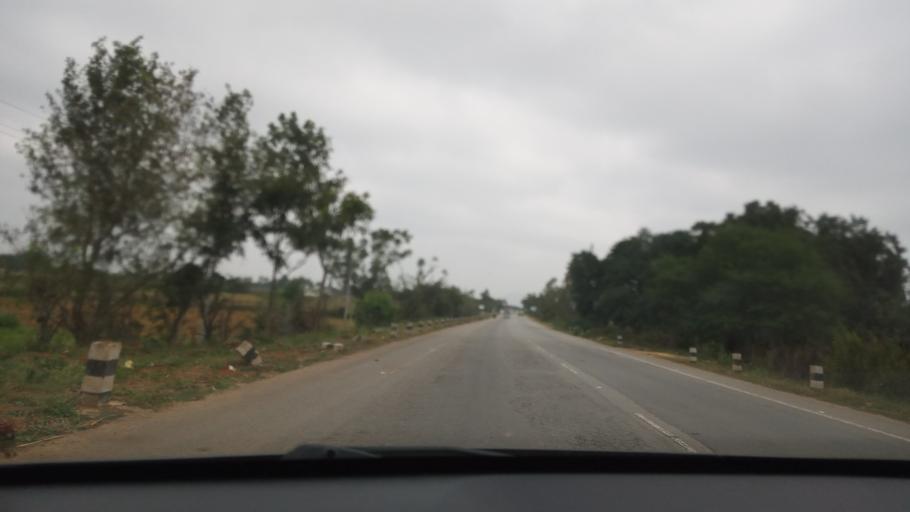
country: IN
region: Karnataka
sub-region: Chikkaballapur
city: Sidlaghatta
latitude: 13.2793
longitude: 77.9555
